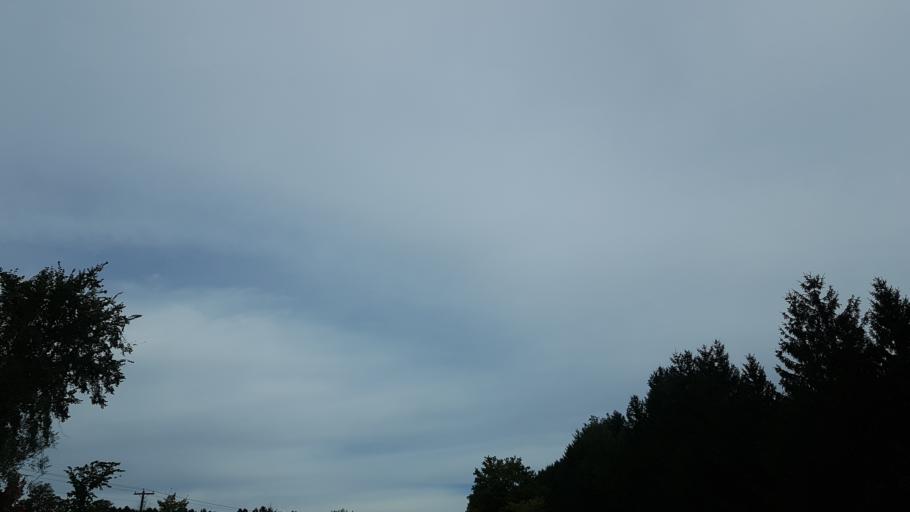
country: CA
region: Ontario
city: Orangeville
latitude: 43.7084
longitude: -80.1227
